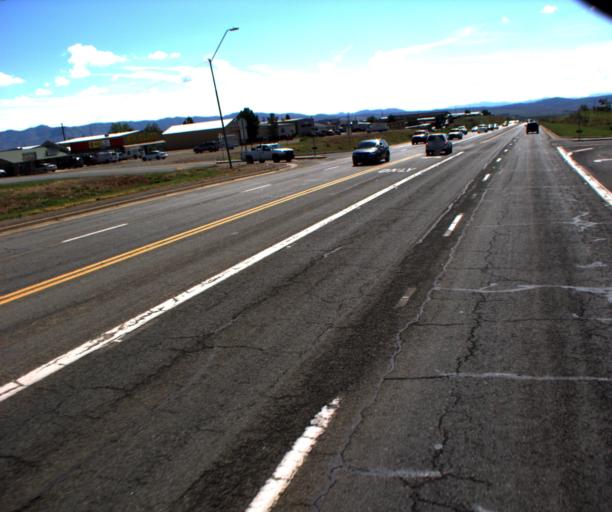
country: US
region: Arizona
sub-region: Yavapai County
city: Prescott Valley
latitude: 34.5843
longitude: -112.3125
